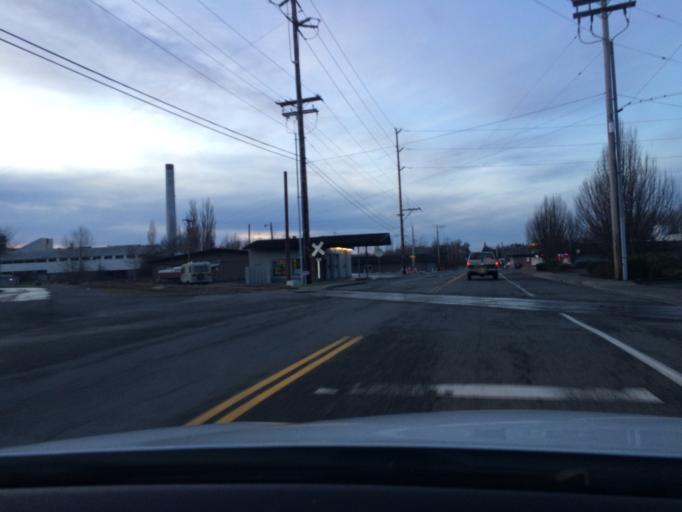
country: US
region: Washington
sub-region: Whatcom County
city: Bellingham
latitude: 48.7682
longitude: -122.5192
